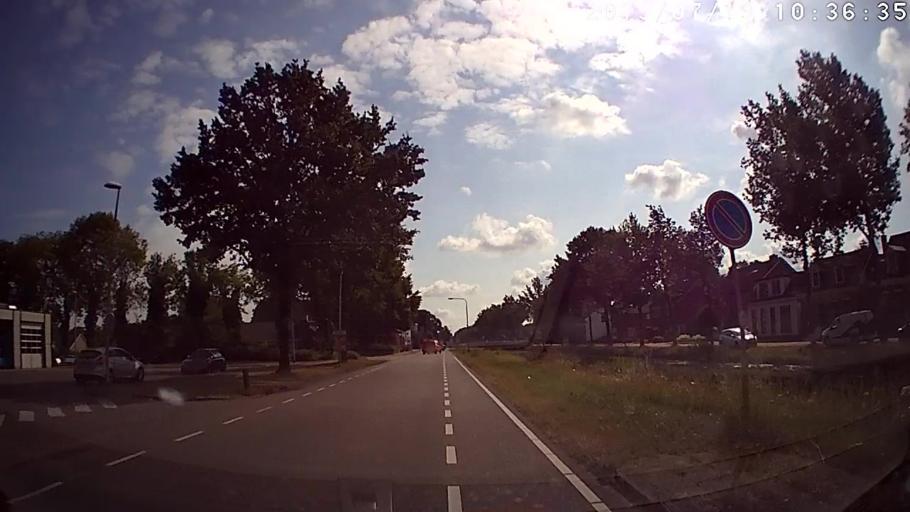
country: NL
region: Drenthe
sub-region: Gemeente Hoogeveen
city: Hoogeveen
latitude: 52.5988
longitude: 6.4490
